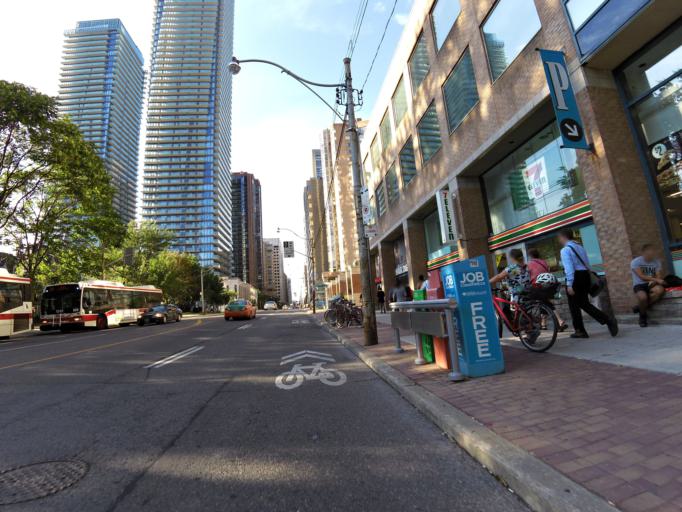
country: CA
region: Ontario
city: Toronto
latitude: 43.6656
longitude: -79.3876
